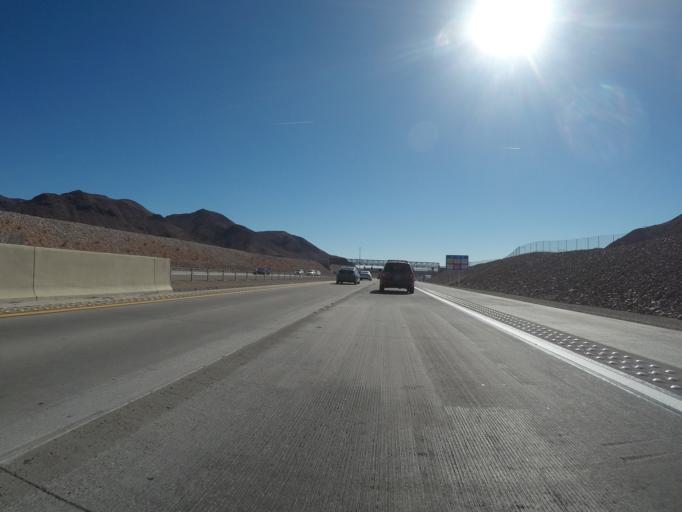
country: US
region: Nevada
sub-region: Clark County
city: Henderson
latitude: 35.9837
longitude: -114.9197
